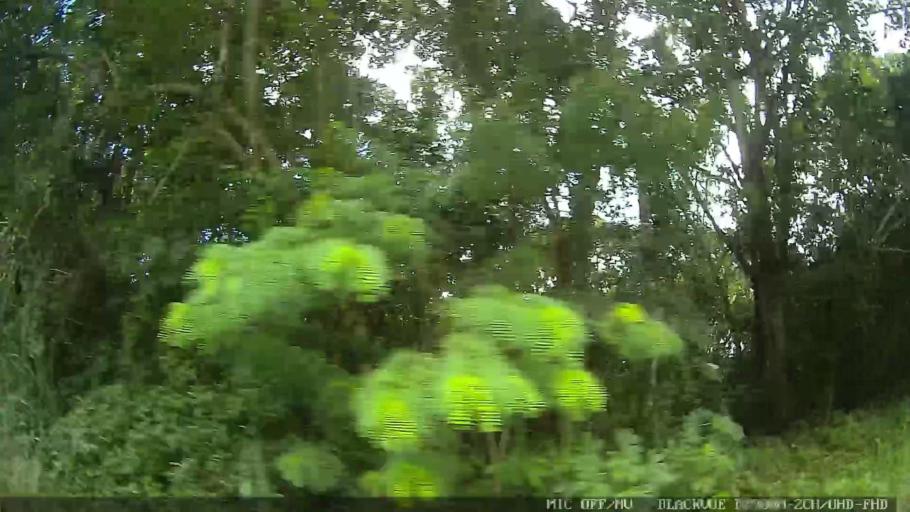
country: BR
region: Sao Paulo
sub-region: Iguape
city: Iguape
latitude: -24.6738
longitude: -47.4496
